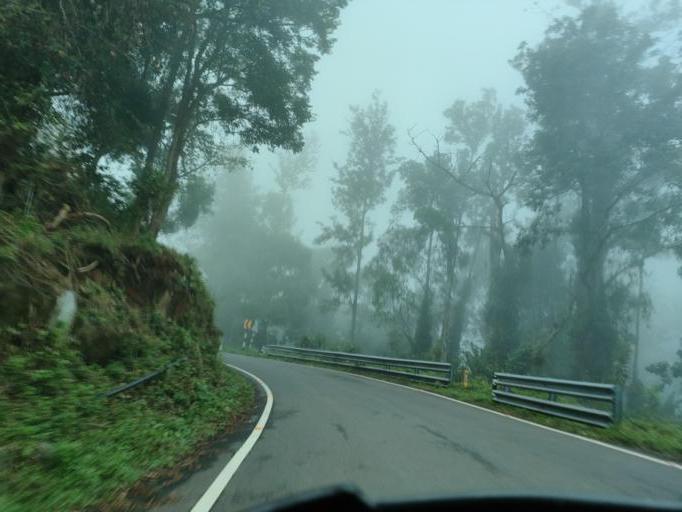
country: IN
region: Tamil Nadu
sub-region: Dindigul
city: Ayakudi
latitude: 10.3557
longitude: 77.5646
